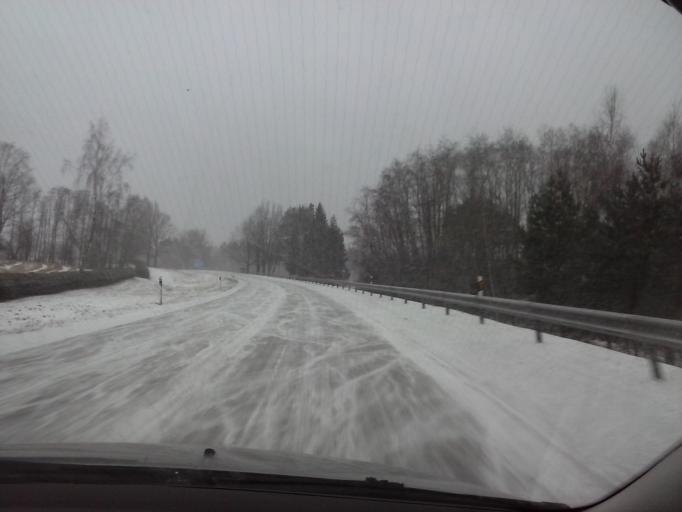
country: EE
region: Valgamaa
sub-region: Torva linn
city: Torva
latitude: 58.0183
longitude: 26.1627
